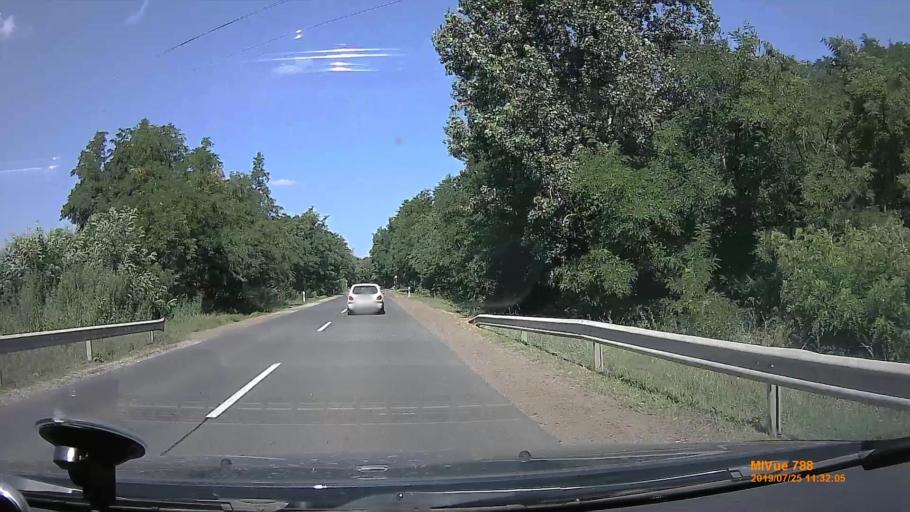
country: HU
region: Szabolcs-Szatmar-Bereg
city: Nyiregyhaza
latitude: 47.9127
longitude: 21.7763
